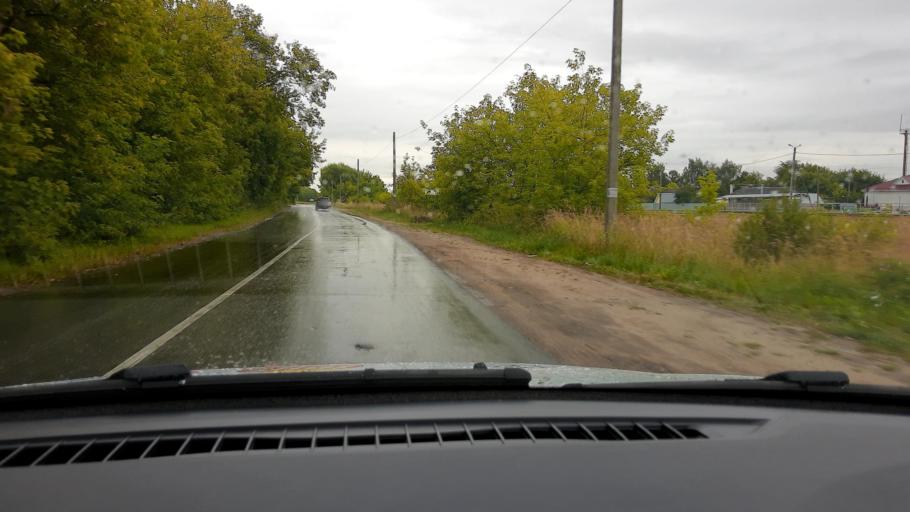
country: RU
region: Nizjnij Novgorod
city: Bogorodsk
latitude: 56.1150
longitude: 43.5216
